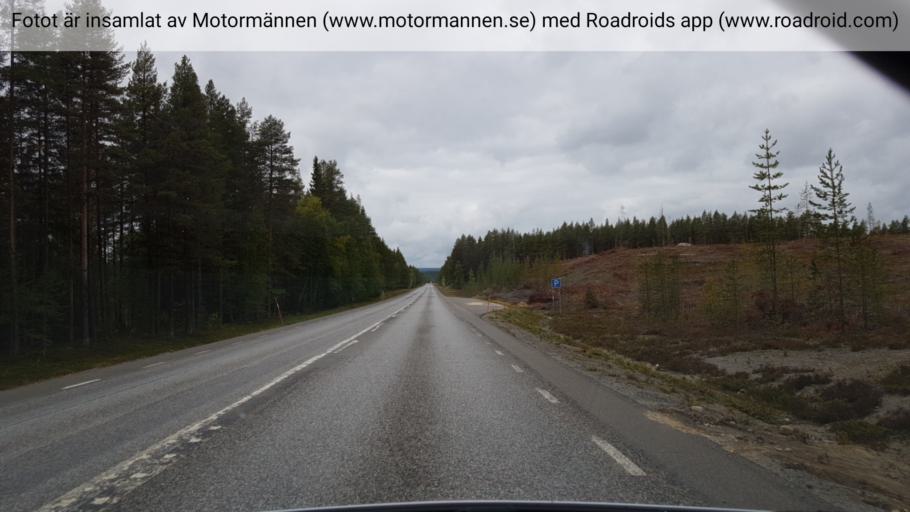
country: SE
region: Vaesterbotten
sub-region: Norsjo Kommun
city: Norsjoe
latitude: 64.9832
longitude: 19.5259
